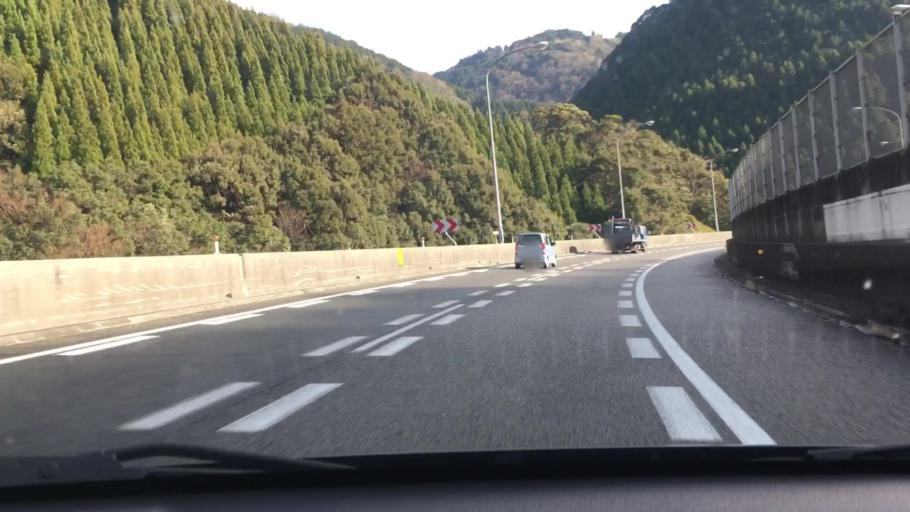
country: JP
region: Kumamoto
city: Hitoyoshi
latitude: 32.3261
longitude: 130.7573
